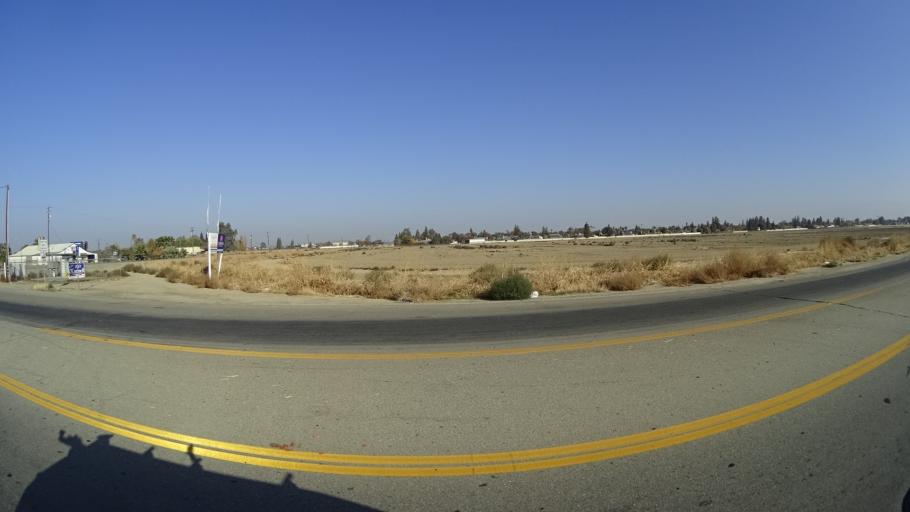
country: US
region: California
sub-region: Kern County
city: Greenfield
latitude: 35.2666
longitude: -119.0203
